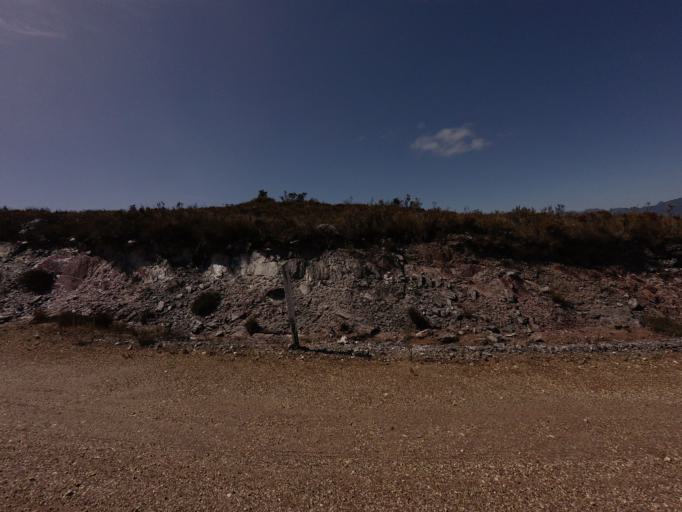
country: AU
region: Tasmania
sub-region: Huon Valley
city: Geeveston
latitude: -43.0380
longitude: 146.2747
